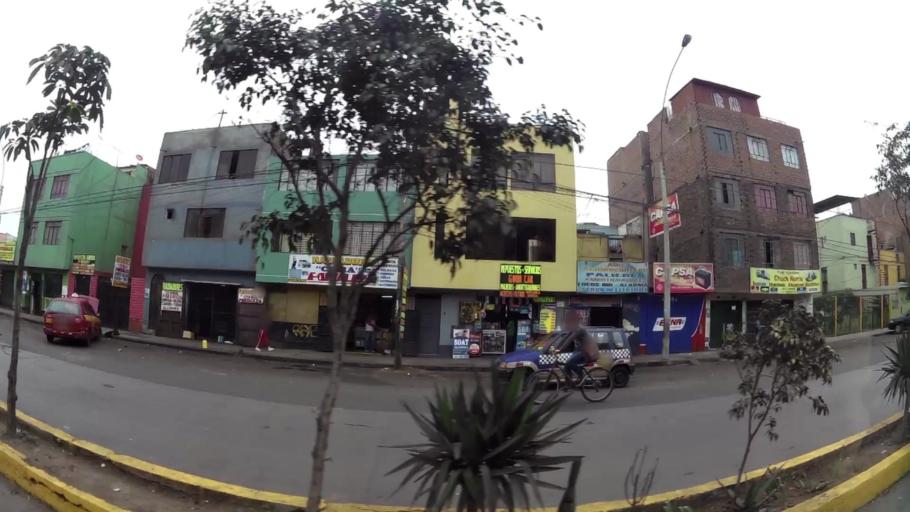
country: PE
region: Lima
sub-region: Lima
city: San Luis
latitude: -12.0779
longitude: -77.0178
